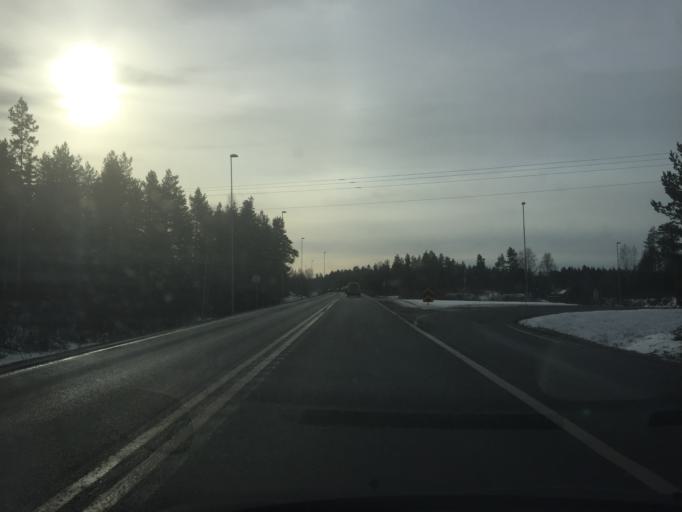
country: NO
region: Hedmark
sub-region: Stange
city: Stange
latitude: 60.7155
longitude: 11.2841
